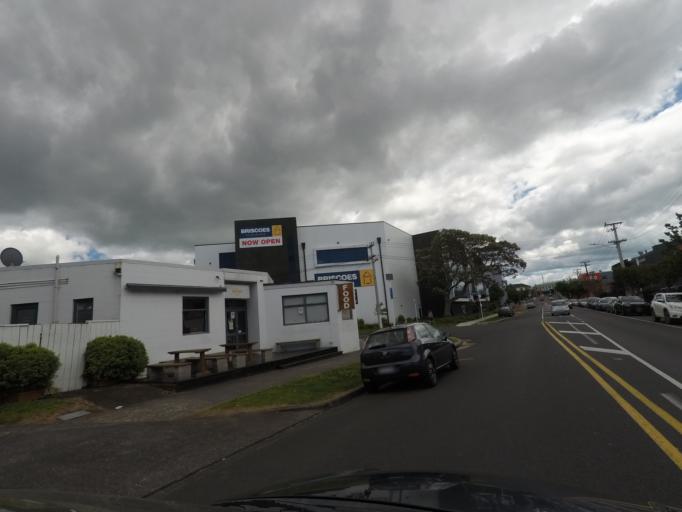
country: NZ
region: Auckland
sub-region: Auckland
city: Auckland
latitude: -36.8762
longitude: 174.7358
